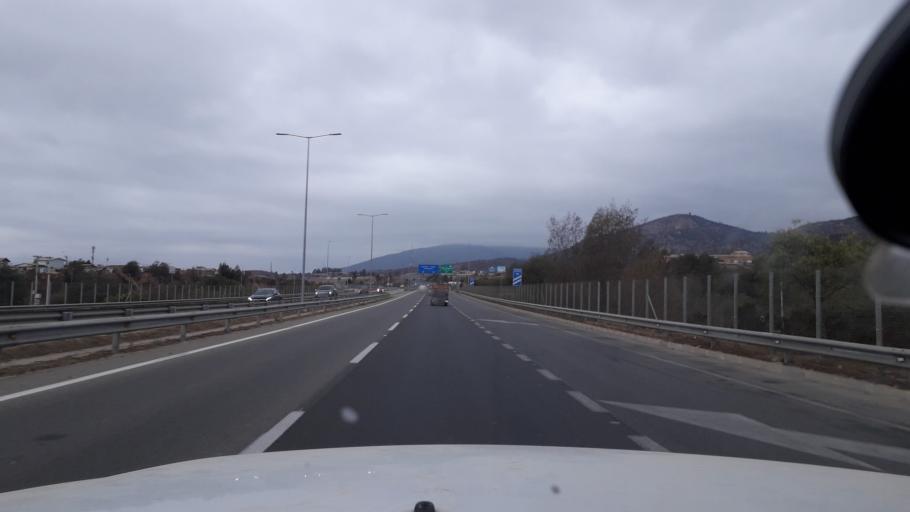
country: CL
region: Valparaiso
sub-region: Provincia de Marga Marga
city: Villa Alemana
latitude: -33.0687
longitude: -71.3729
